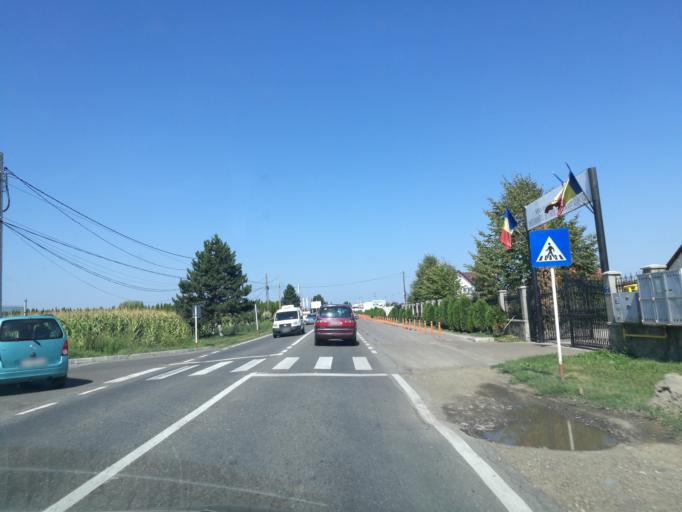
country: RO
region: Suceava
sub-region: Comuna Burla
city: Burla
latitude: 47.8227
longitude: 25.9434
